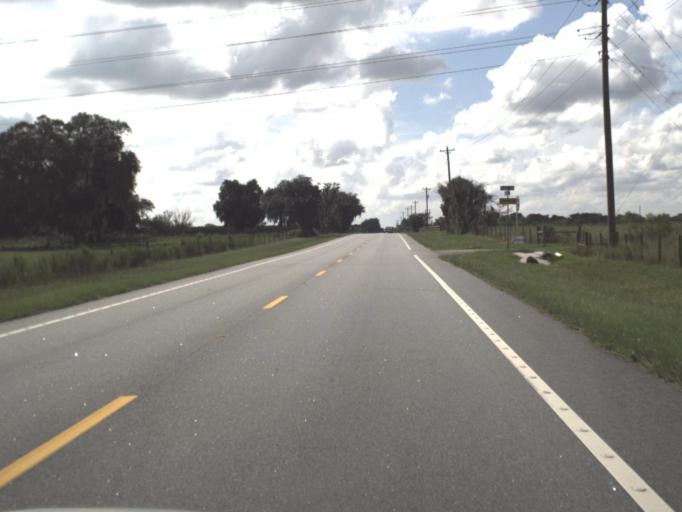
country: US
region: Florida
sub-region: Hardee County
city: Wauchula
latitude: 27.4601
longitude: -82.0915
